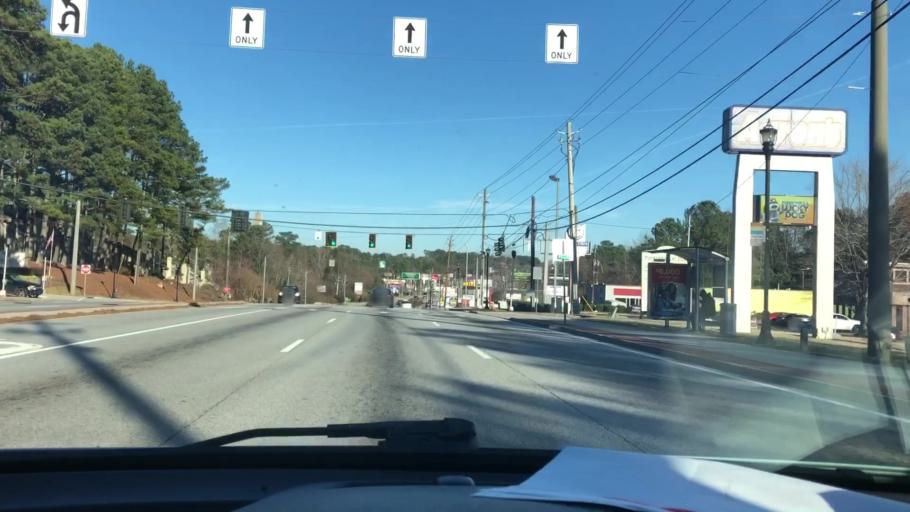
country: US
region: Georgia
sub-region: DeKalb County
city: Clarkston
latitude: 33.7997
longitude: -84.2176
